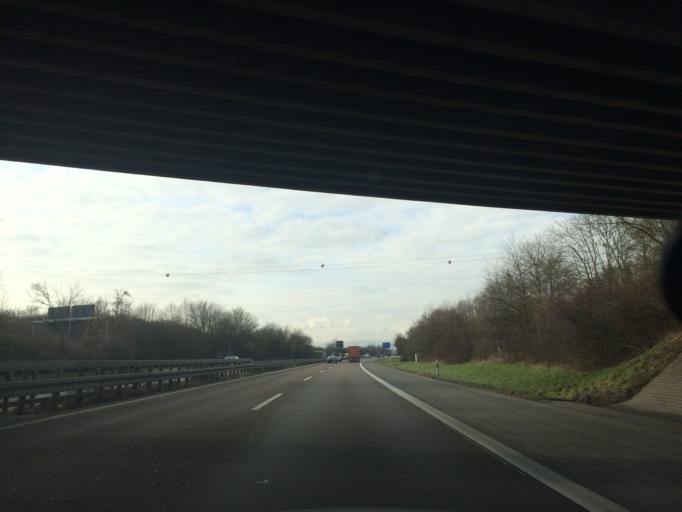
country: DE
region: Hesse
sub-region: Regierungsbezirk Darmstadt
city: Wiesbaden
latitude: 50.0501
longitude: 8.2902
